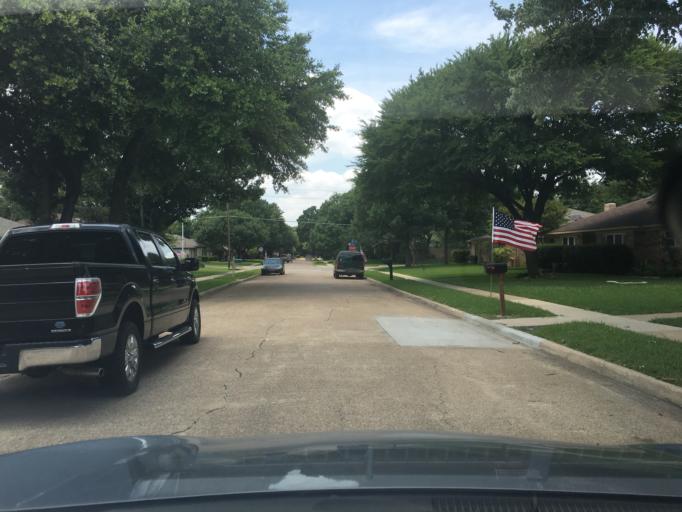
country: US
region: Texas
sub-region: Dallas County
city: Richardson
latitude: 32.9583
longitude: -96.6903
